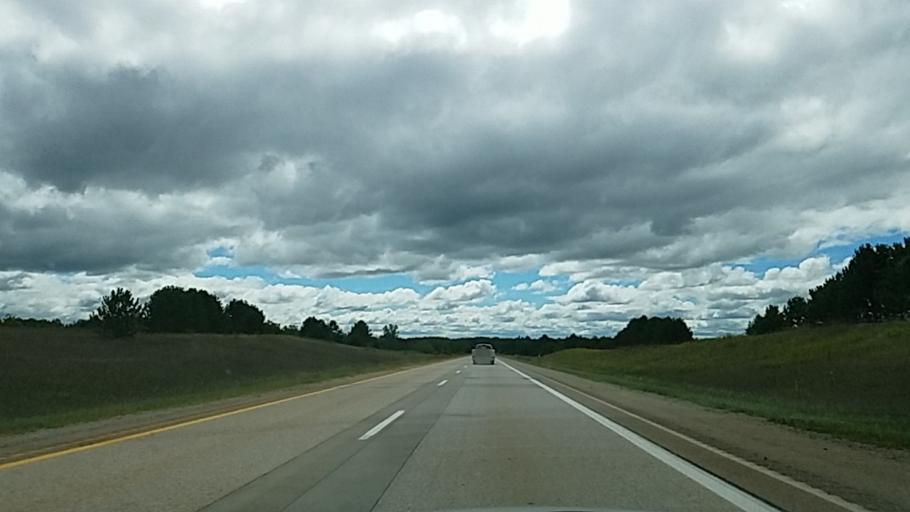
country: US
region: Michigan
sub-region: Ogemaw County
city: West Branch
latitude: 44.2322
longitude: -84.2134
